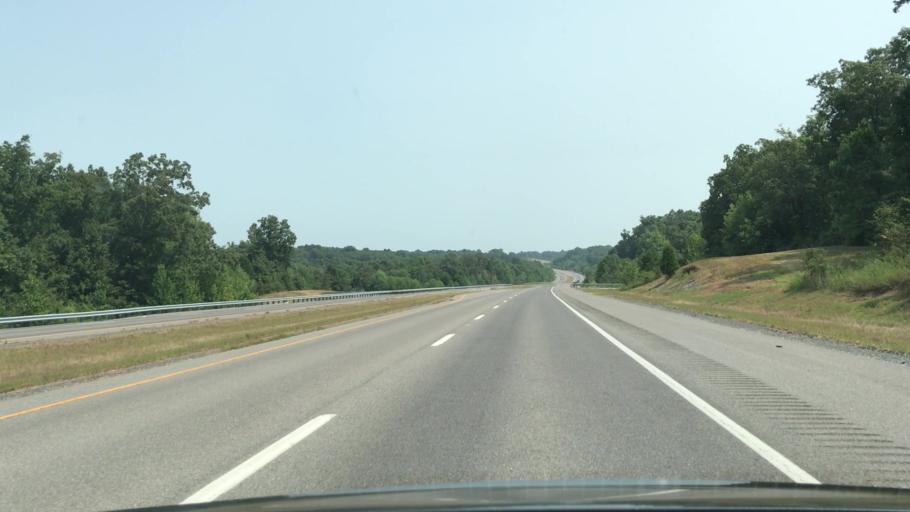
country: US
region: Kentucky
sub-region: Calloway County
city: Murray
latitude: 36.7490
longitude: -88.1585
